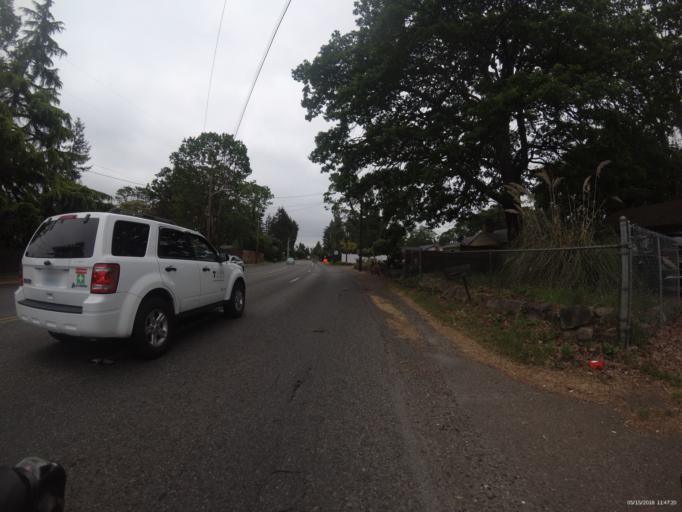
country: US
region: Washington
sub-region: Pierce County
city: Lakewood
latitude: 47.1791
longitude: -122.5276
